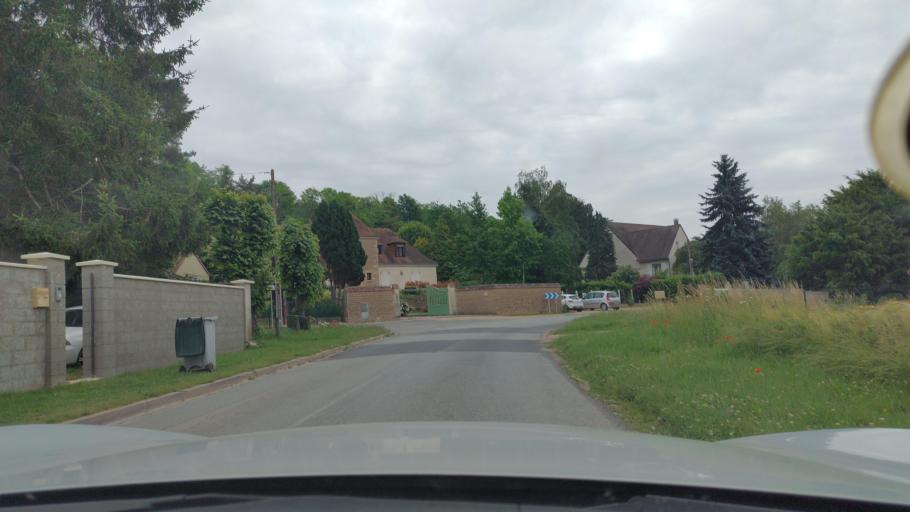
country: FR
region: Picardie
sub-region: Departement de l'Oise
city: Betz
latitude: 49.1019
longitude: 2.9586
